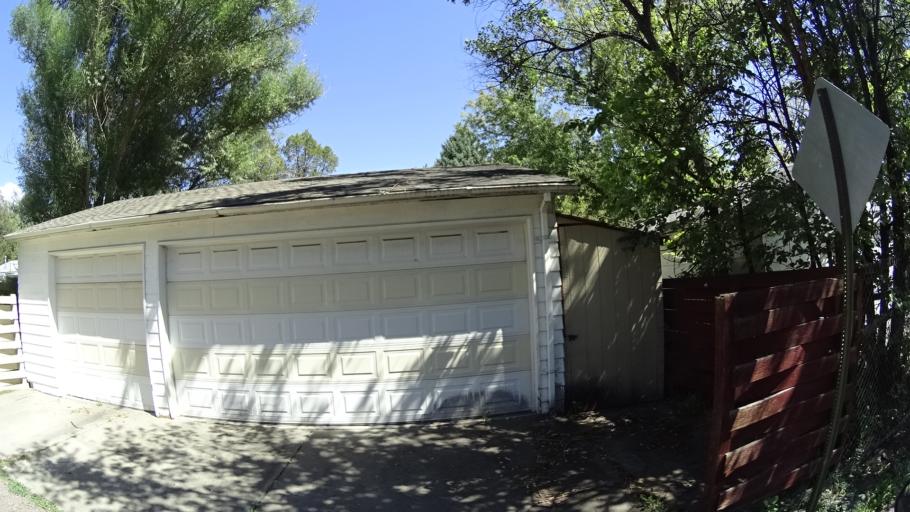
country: US
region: Colorado
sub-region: El Paso County
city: Manitou Springs
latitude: 38.8613
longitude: -104.8699
